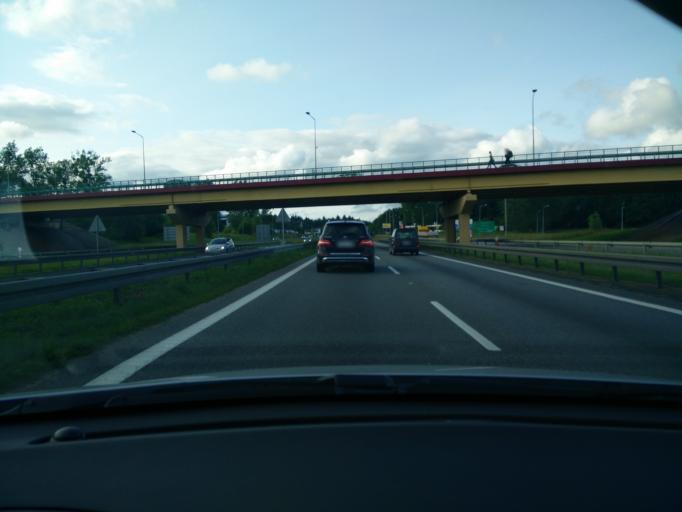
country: PL
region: Pomeranian Voivodeship
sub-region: Gdynia
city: Wielki Kack
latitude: 54.4291
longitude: 18.4880
